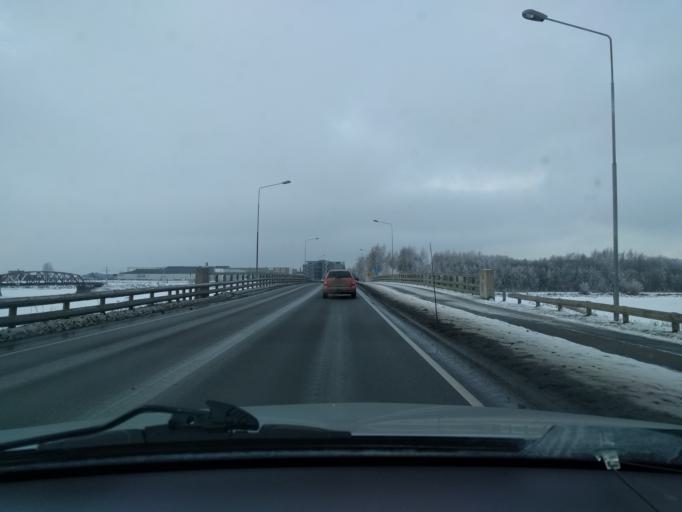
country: NO
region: Hedmark
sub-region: Hamar
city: Hamar
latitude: 60.7876
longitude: 11.0991
